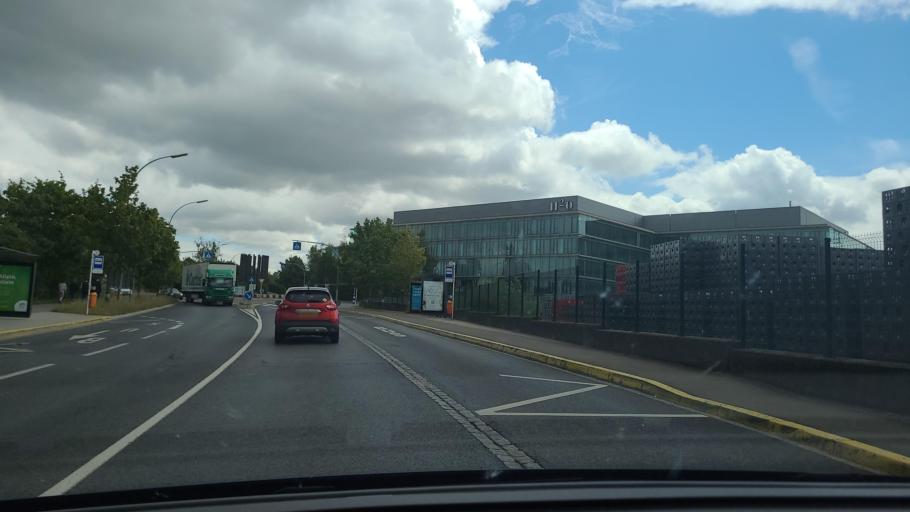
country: LU
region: Luxembourg
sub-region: Canton de Luxembourg
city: Hesperange
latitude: 49.5770
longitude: 6.1349
